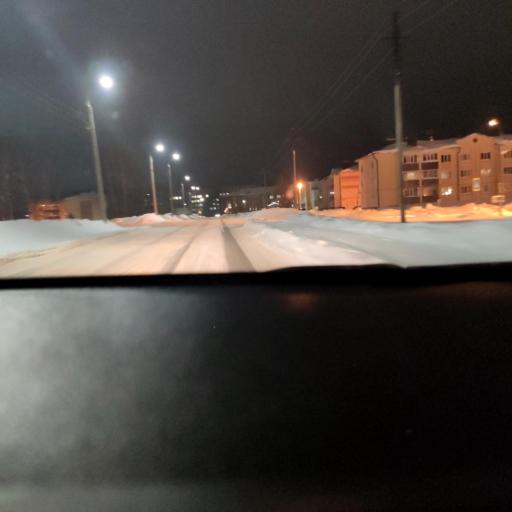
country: RU
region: Tatarstan
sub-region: Chistopol'skiy Rayon
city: Chistopol'
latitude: 55.3603
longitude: 50.5832
